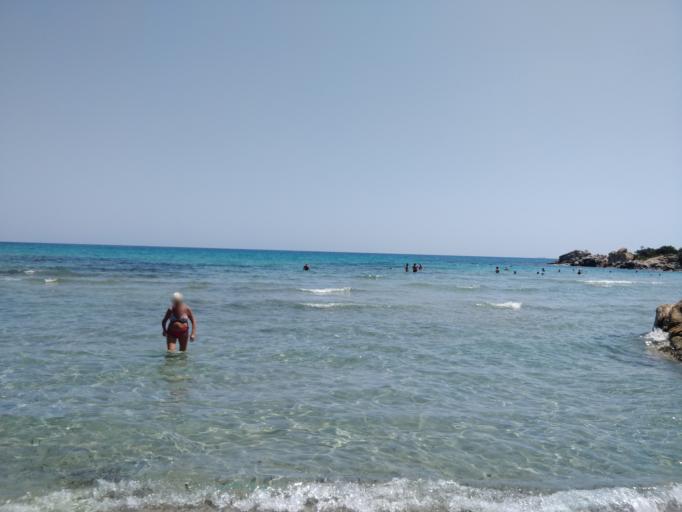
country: IT
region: Sardinia
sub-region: Provincia di Ogliastra
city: Tortoli
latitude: 39.8811
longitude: 9.6815
